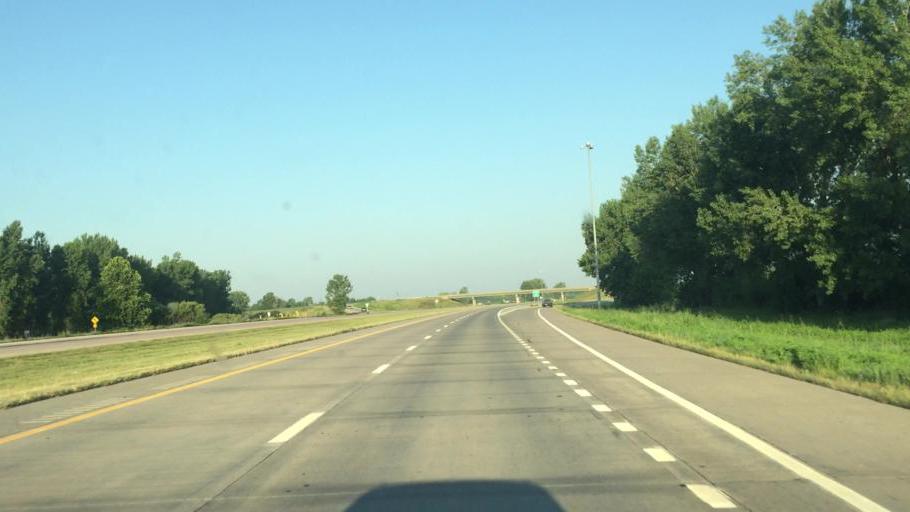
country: US
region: Kansas
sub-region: Doniphan County
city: Elwood
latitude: 39.7423
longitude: -94.8878
